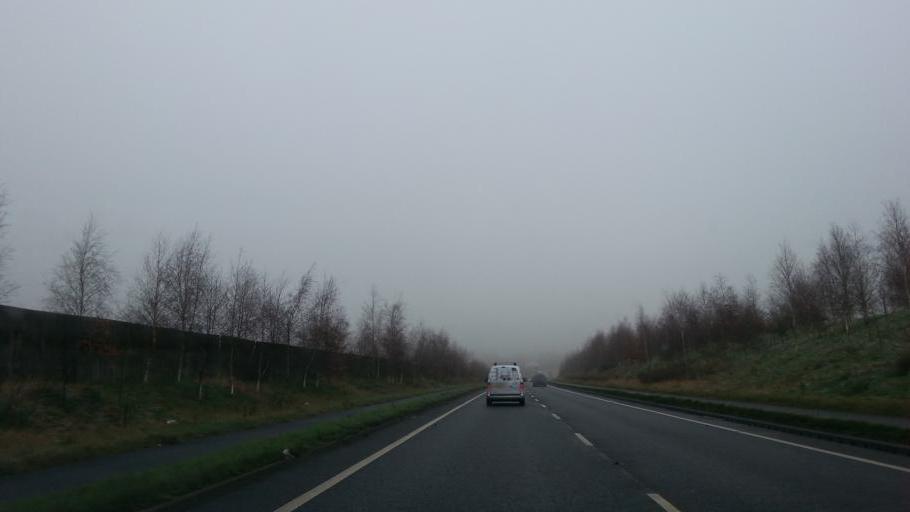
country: GB
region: England
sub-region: Cheshire East
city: Alderley Edge
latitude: 53.3031
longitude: -2.2479
